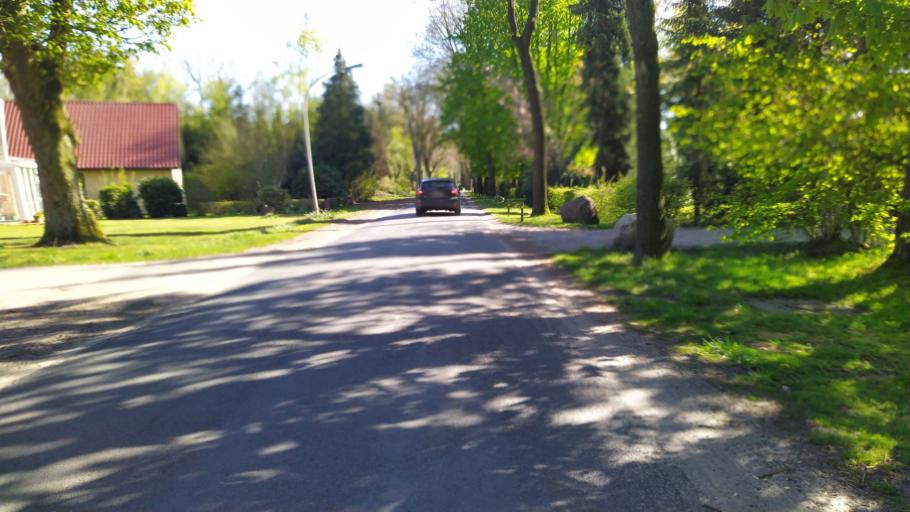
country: DE
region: Lower Saxony
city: Heeslingen
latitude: 53.3045
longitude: 9.3838
